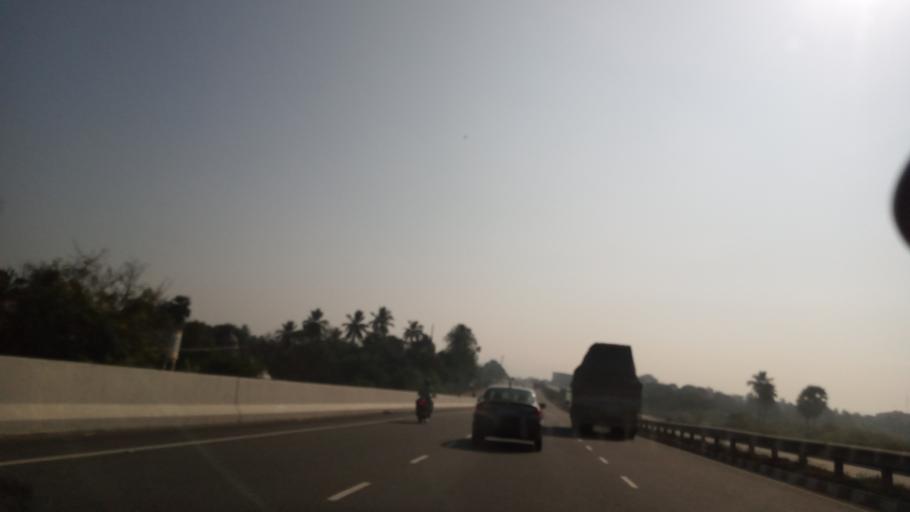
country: IN
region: Tamil Nadu
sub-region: Vellore
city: Vellore
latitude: 12.9150
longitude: 79.0678
